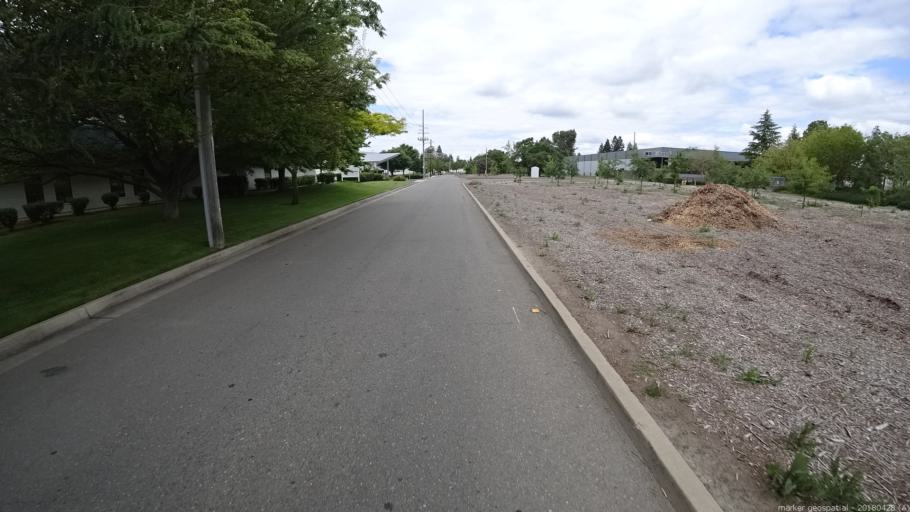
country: US
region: California
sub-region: Yolo County
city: West Sacramento
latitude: 38.5609
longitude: -121.5765
